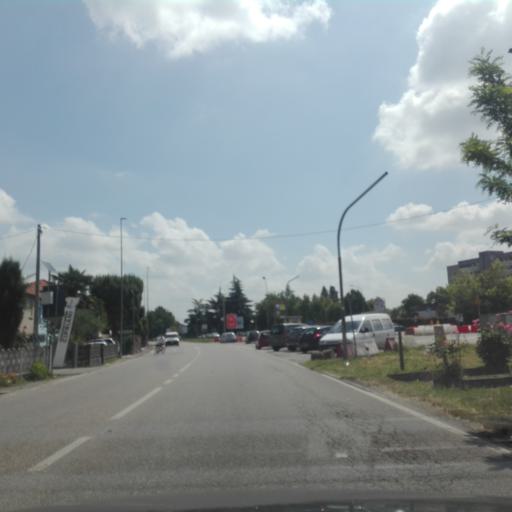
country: IT
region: Veneto
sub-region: Provincia di Rovigo
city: Rovigo
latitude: 45.0745
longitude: 11.8145
